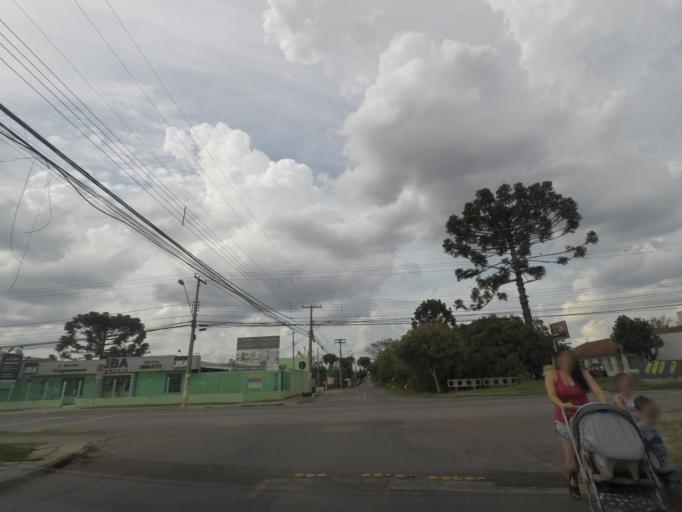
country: BR
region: Parana
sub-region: Sao Jose Dos Pinhais
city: Sao Jose dos Pinhais
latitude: -25.4889
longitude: -49.2507
